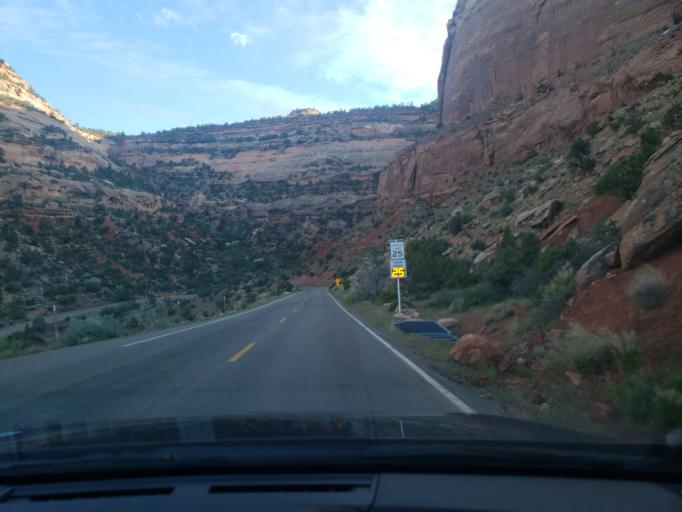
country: US
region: Colorado
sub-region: Mesa County
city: Fruita
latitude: 39.1101
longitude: -108.7356
